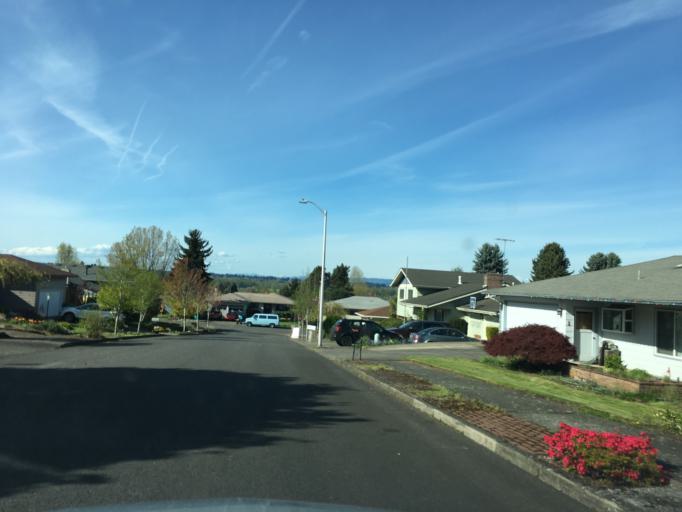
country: US
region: Oregon
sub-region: Multnomah County
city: Fairview
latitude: 45.5464
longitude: -122.5167
